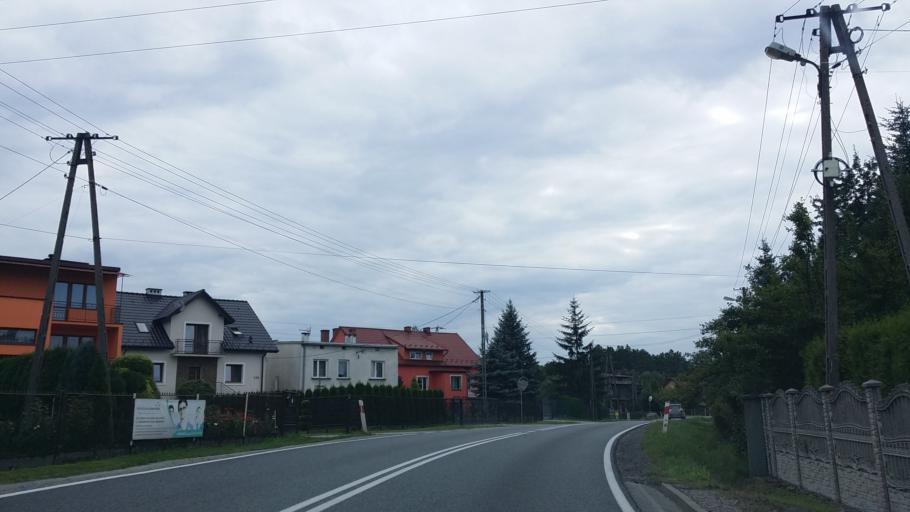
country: PL
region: Lesser Poland Voivodeship
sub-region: Powiat krakowski
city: Krzecin
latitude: 49.9615
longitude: 19.7563
